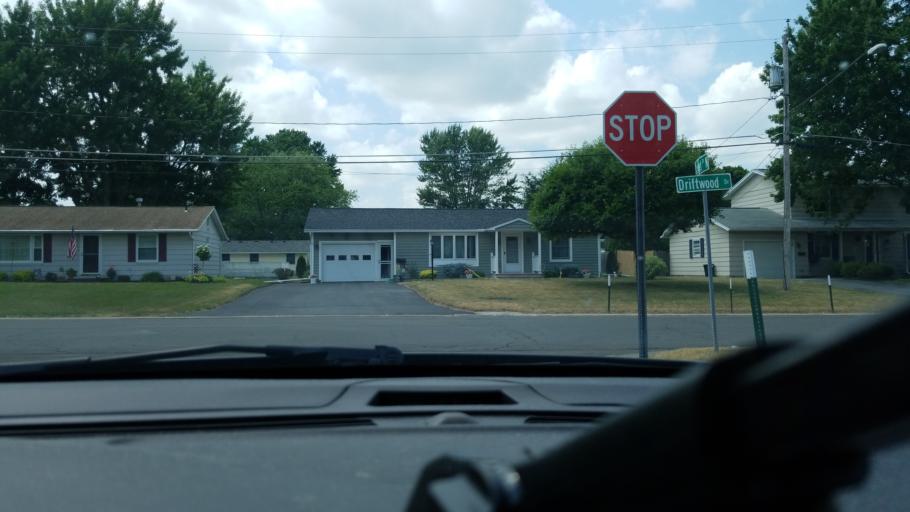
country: US
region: New York
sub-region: Onondaga County
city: Galeville
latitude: 43.1063
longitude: -76.1759
